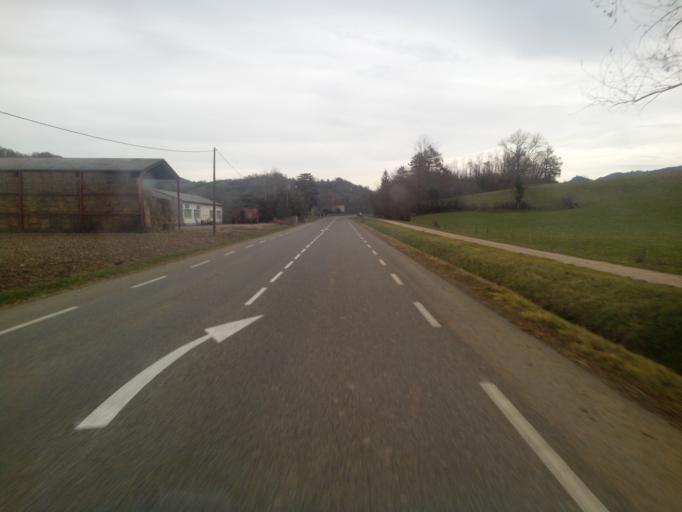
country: FR
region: Midi-Pyrenees
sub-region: Departement de l'Ariege
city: Foix
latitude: 43.0174
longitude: 1.3992
